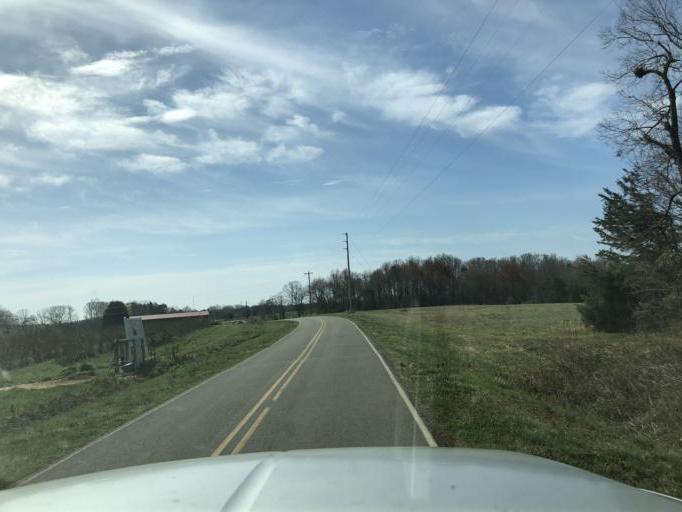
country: US
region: North Carolina
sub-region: Cleveland County
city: Shelby
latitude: 35.4787
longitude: -81.6419
